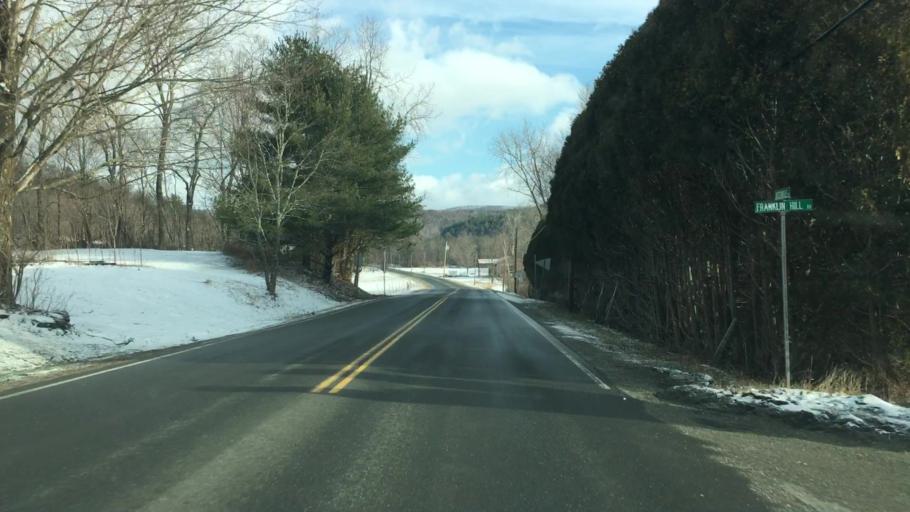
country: US
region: Massachusetts
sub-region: Franklin County
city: Colrain
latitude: 42.7114
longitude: -72.7037
